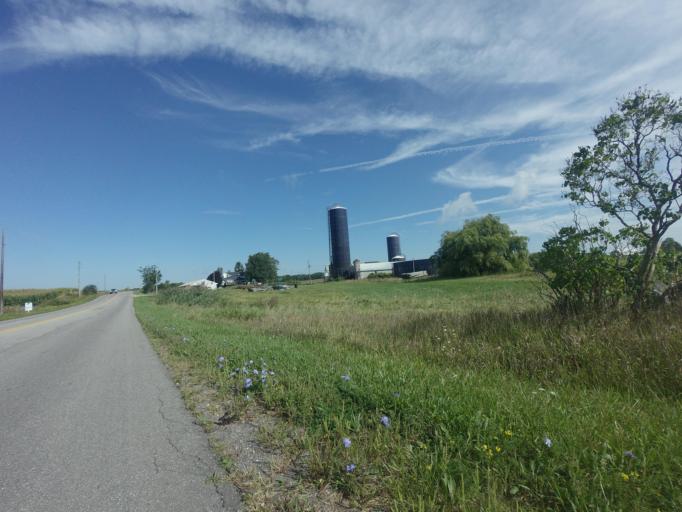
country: CA
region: Ontario
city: Waterloo
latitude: 43.4714
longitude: -80.7226
